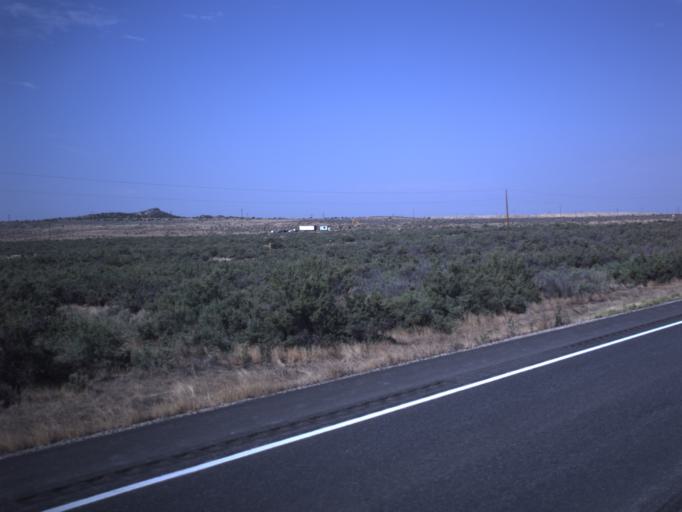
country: US
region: Utah
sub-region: Uintah County
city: Naples
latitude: 40.3060
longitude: -109.2093
